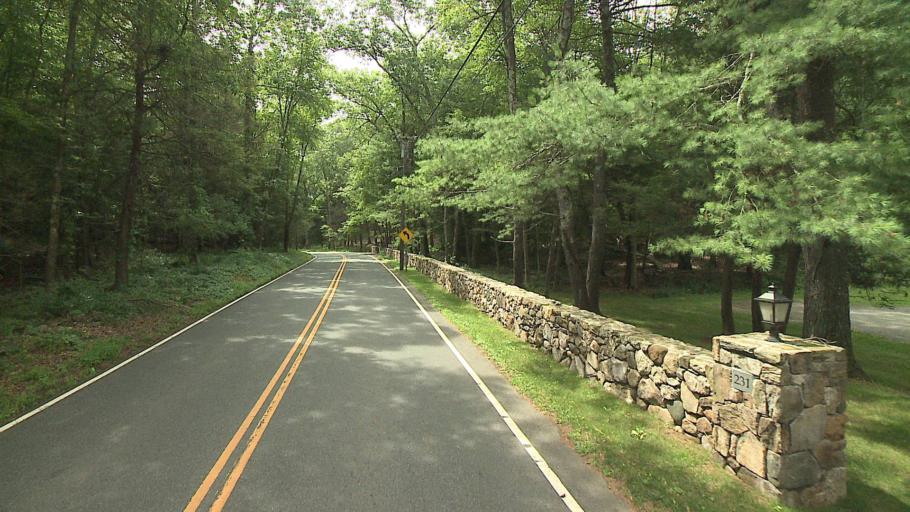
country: US
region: Connecticut
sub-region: Litchfield County
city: New Preston
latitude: 41.6009
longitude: -73.3221
